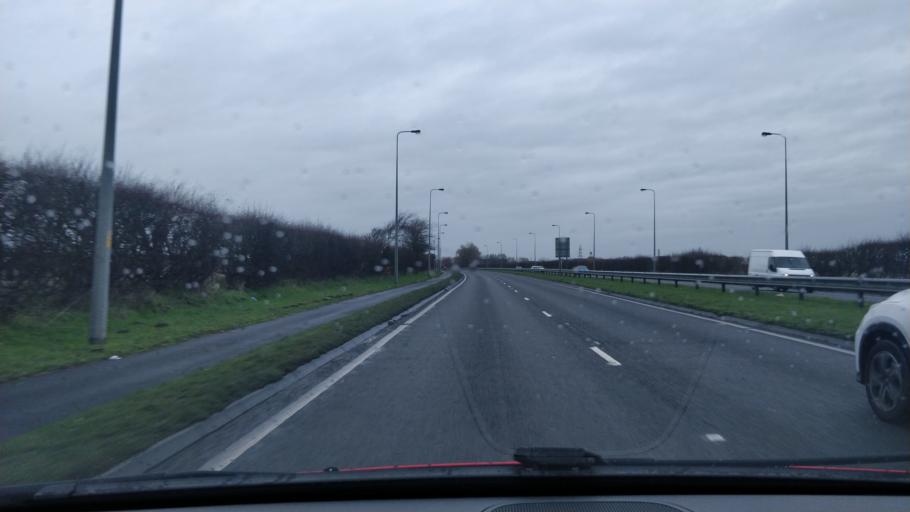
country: GB
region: England
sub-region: Sefton
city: Formby
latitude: 53.5482
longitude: -3.0473
